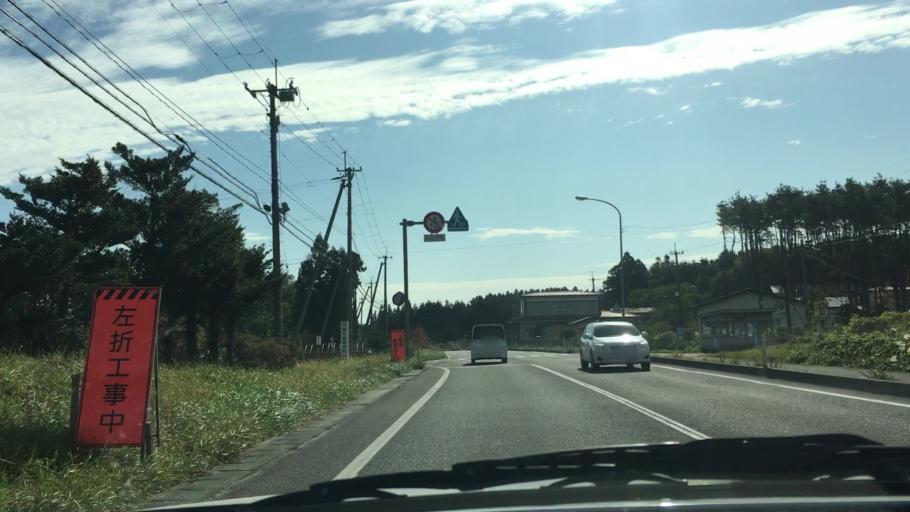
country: JP
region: Aomori
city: Hachinohe
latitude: 40.4289
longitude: 141.6917
